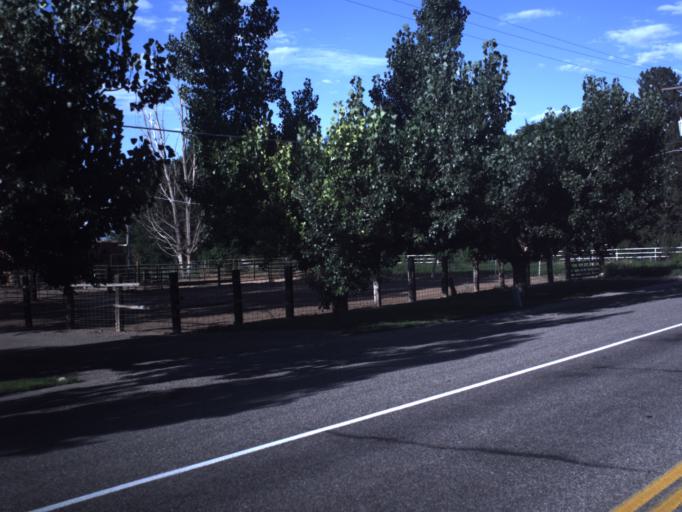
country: US
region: Utah
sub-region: Sevier County
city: Monroe
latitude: 38.6831
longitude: -112.1414
